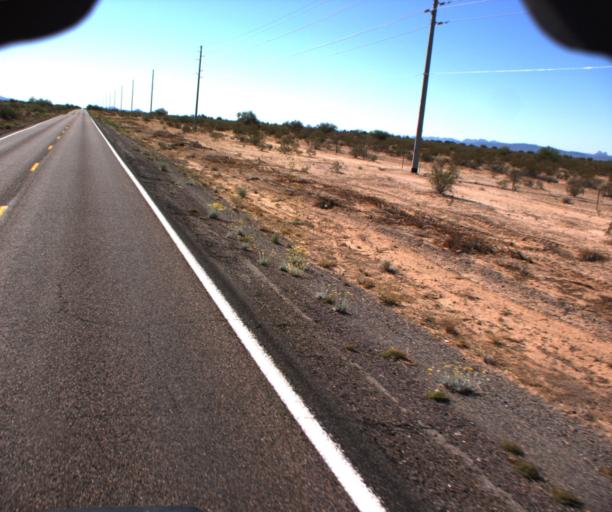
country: US
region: Arizona
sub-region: La Paz County
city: Salome
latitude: 33.8858
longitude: -113.9527
